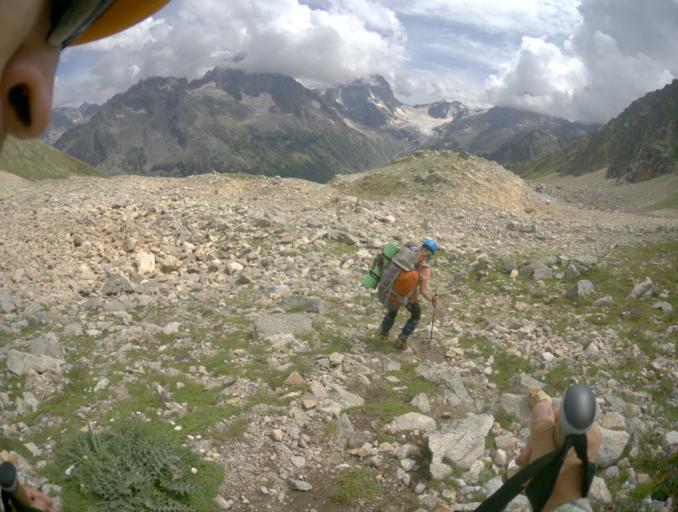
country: RU
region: Karachayevo-Cherkesiya
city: Uchkulan
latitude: 43.2749
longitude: 42.1225
